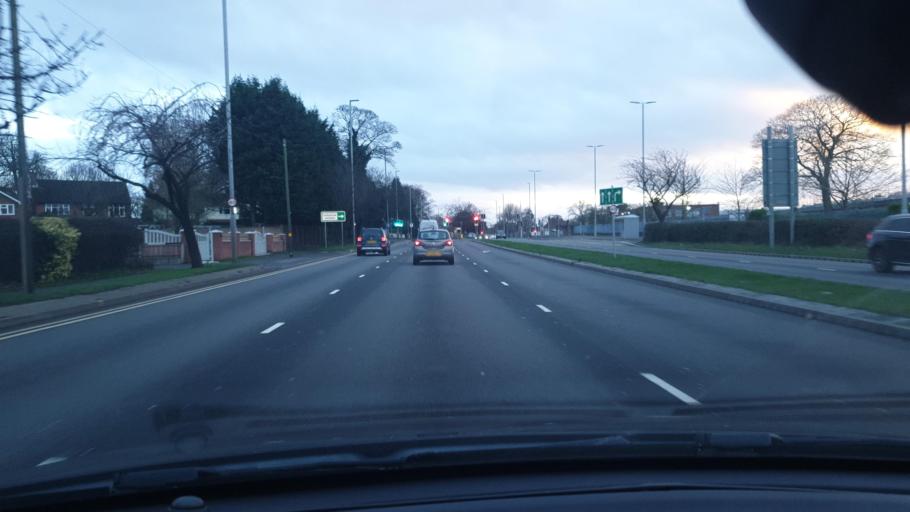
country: GB
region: England
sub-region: Staffordshire
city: Featherstone
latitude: 52.6332
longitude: -2.1249
